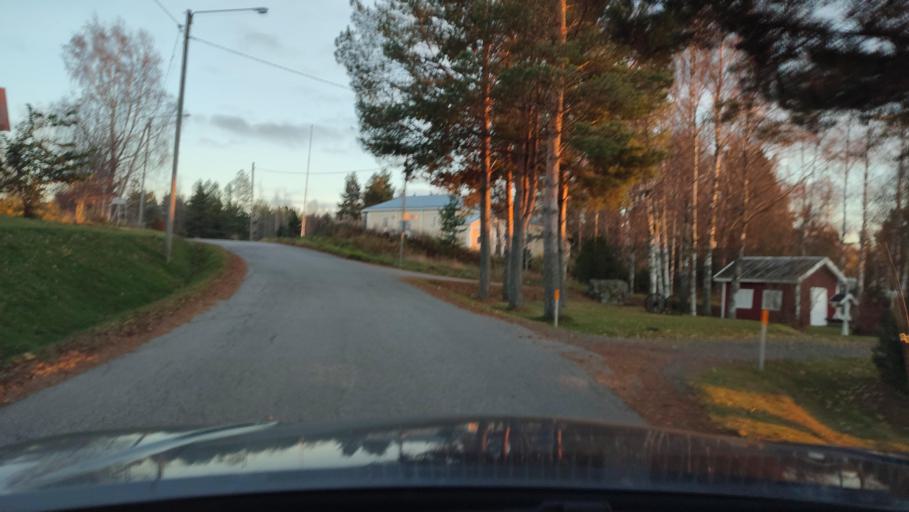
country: FI
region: Ostrobothnia
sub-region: Sydosterbotten
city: Kristinestad
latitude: 62.2992
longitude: 21.4572
